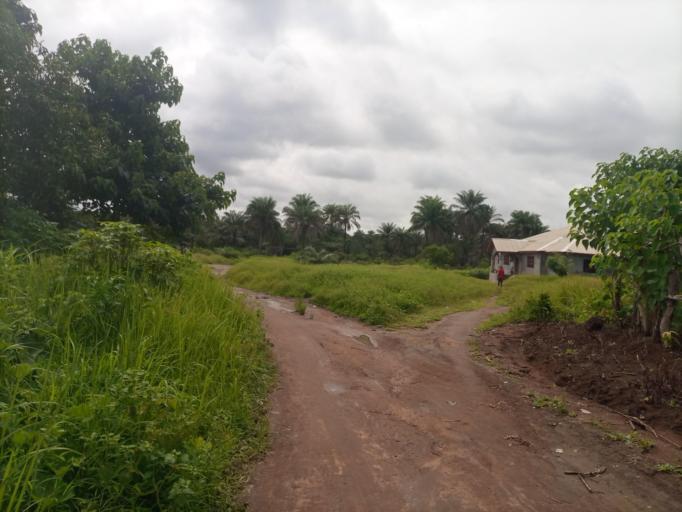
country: SL
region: Northern Province
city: Sawkta
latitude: 8.6248
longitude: -13.1970
